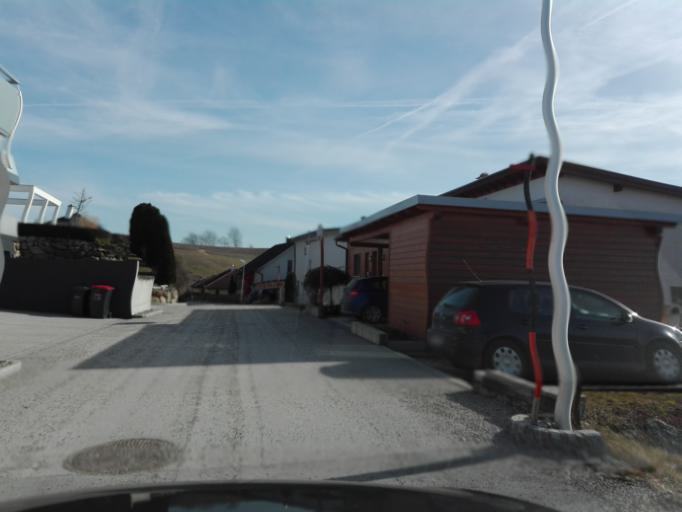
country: AT
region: Upper Austria
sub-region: Politischer Bezirk Perg
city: Perg
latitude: 48.2582
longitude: 14.5945
